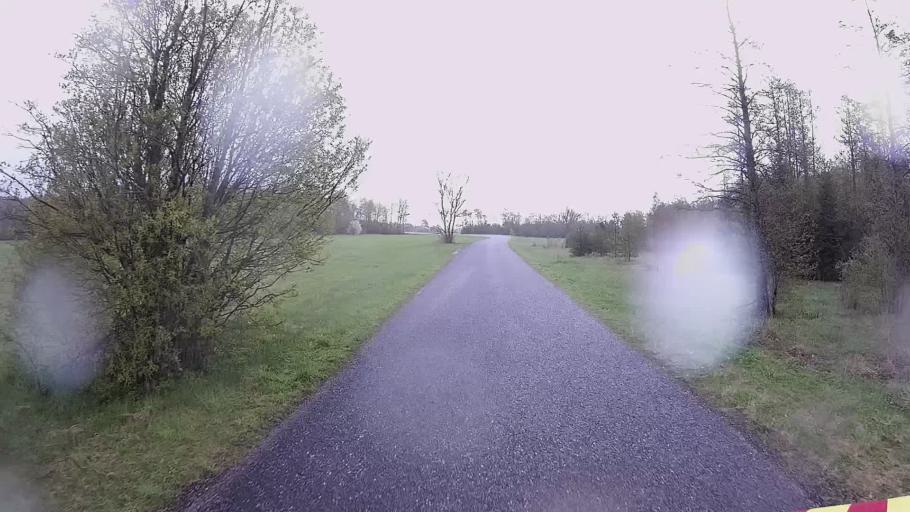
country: EE
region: Hiiumaa
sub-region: Kaerdla linn
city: Kardla
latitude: 58.6963
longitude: 22.5501
